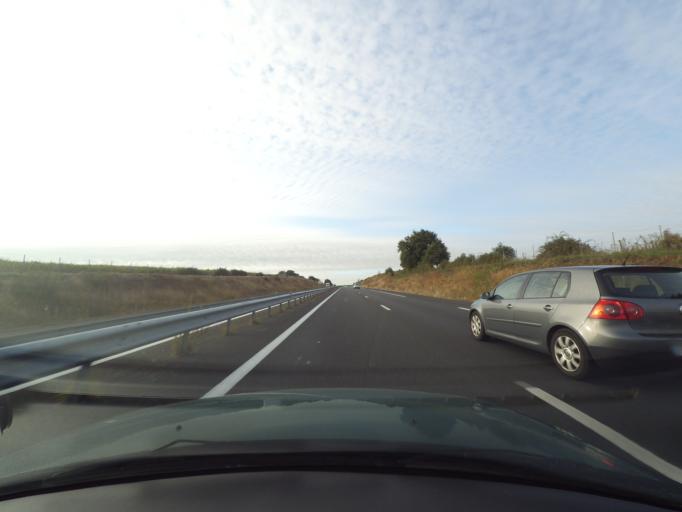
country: FR
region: Pays de la Loire
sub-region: Departement de Maine-et-Loire
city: La Tessoualle
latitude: 47.0108
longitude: -0.8706
